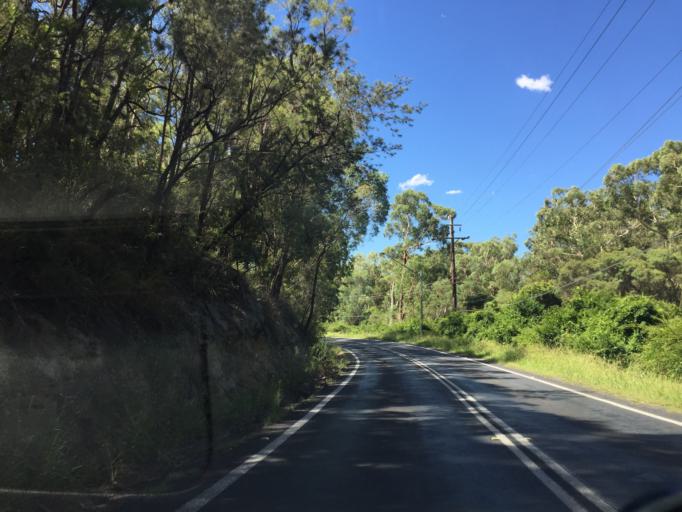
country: AU
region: New South Wales
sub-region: The Hills Shire
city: Beaumont Hills
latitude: -33.6962
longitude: 150.9691
